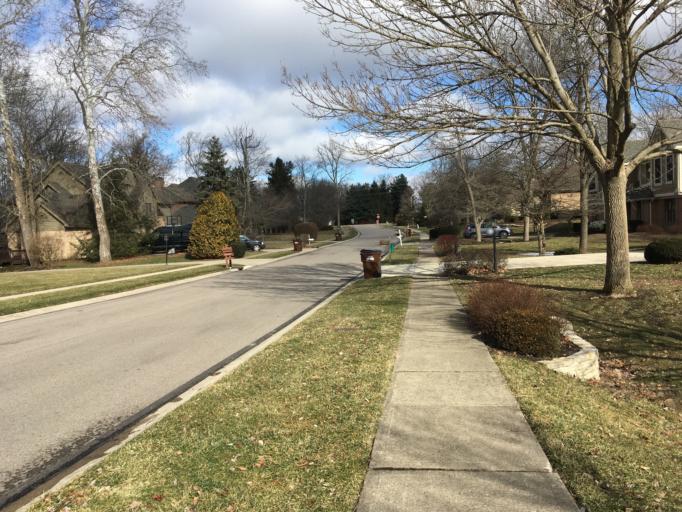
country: US
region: Ohio
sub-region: Montgomery County
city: Centerville
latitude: 39.5969
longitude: -84.1492
